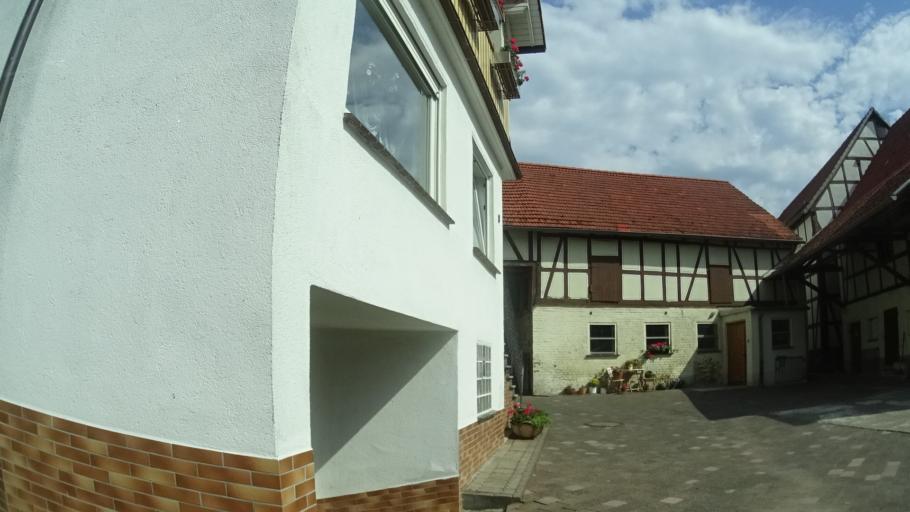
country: DE
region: Hesse
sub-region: Regierungsbezirk Kassel
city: Frankenau
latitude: 51.1287
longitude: 9.0166
